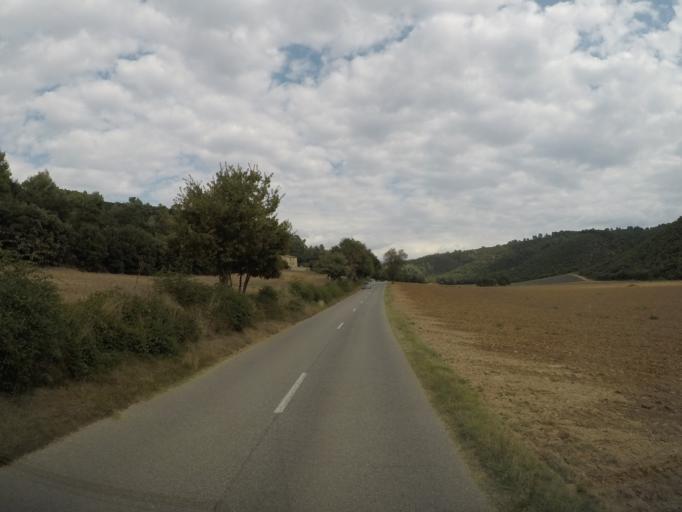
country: FR
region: Provence-Alpes-Cote d'Azur
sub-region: Departement des Alpes-de-Haute-Provence
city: Greoux-les-Bains
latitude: 43.7916
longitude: 5.9202
